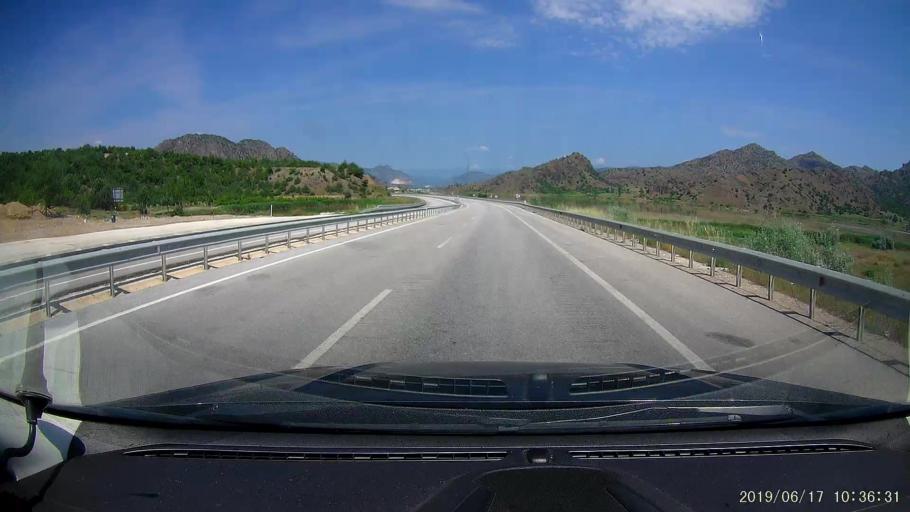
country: TR
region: Corum
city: Osmancik
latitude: 40.9803
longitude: 34.6796
